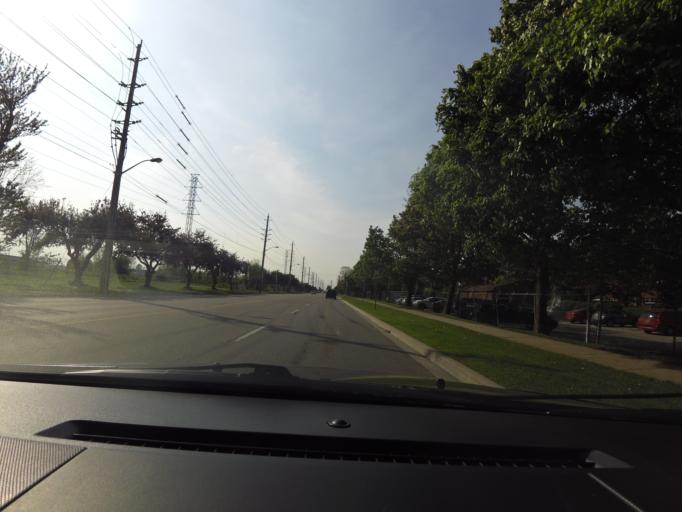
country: CA
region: Ontario
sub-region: Wellington County
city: Guelph
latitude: 43.5549
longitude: -80.2825
